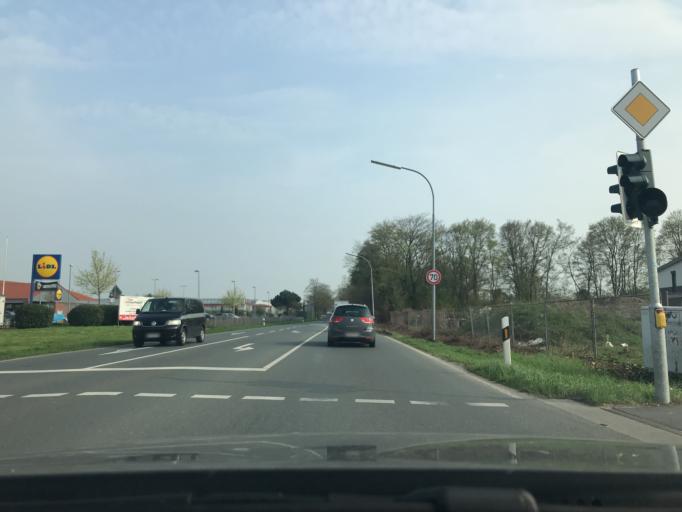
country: DE
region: North Rhine-Westphalia
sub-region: Regierungsbezirk Dusseldorf
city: Kevelaer
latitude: 51.5889
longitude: 6.2465
